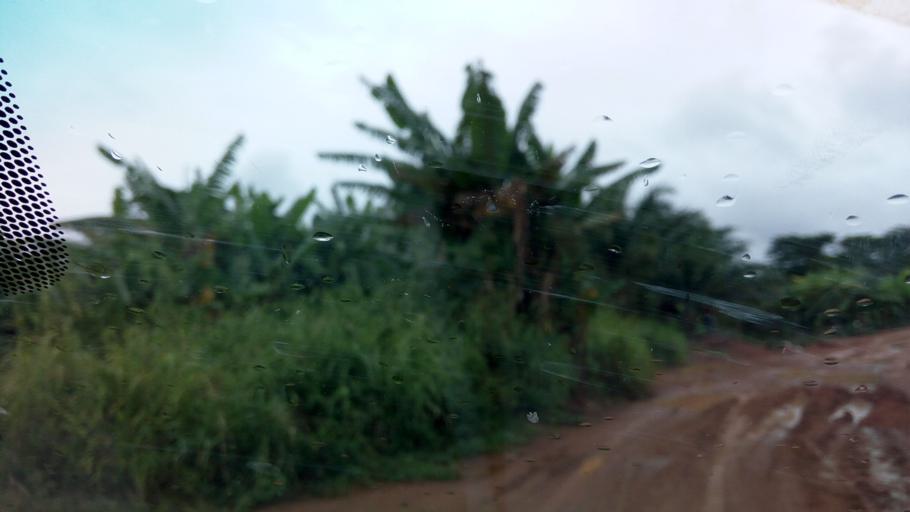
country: ZM
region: Luapula
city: Nchelenge
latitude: -9.0989
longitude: 28.3090
